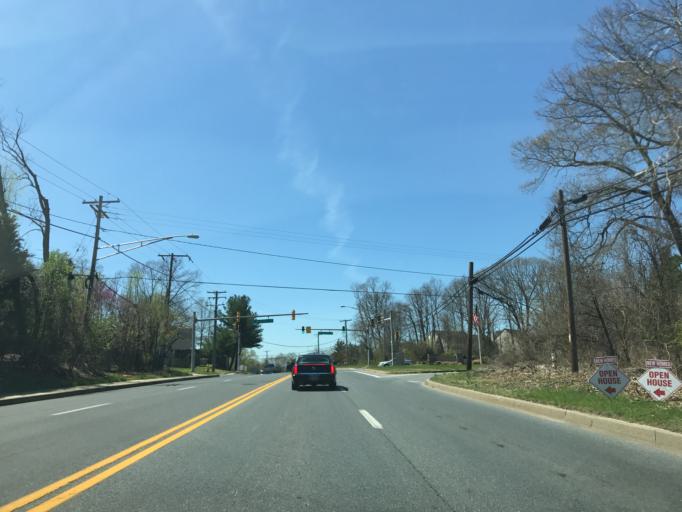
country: US
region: Maryland
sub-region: Anne Arundel County
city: South Gate
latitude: 39.1406
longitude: -76.6523
